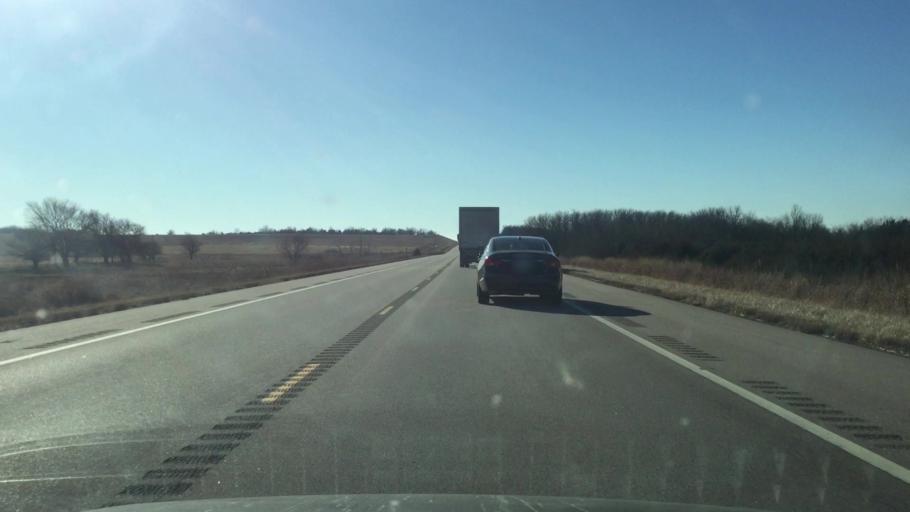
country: US
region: Kansas
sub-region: Allen County
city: Iola
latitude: 38.0226
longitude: -95.3806
